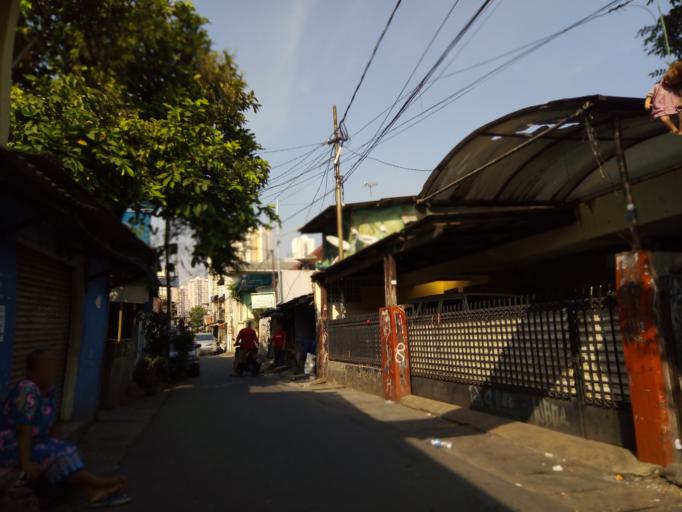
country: ID
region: Jakarta Raya
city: Jakarta
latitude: -6.2099
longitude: 106.8408
